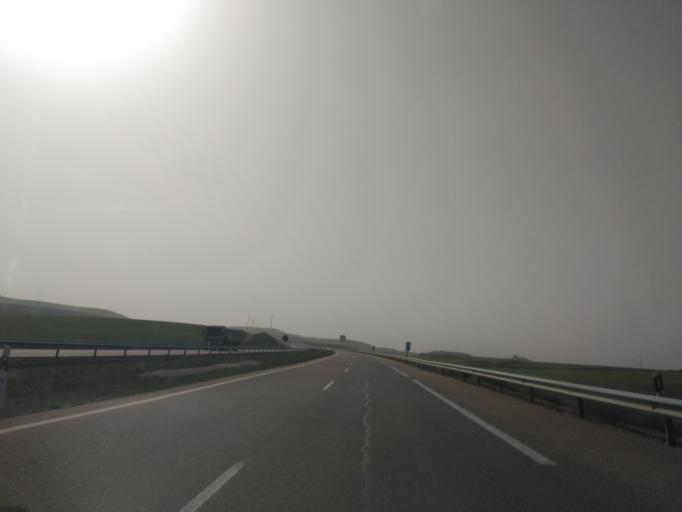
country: ES
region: Castille and Leon
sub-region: Provincia de Palencia
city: Monzon de Campos
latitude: 42.1269
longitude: -4.4779
